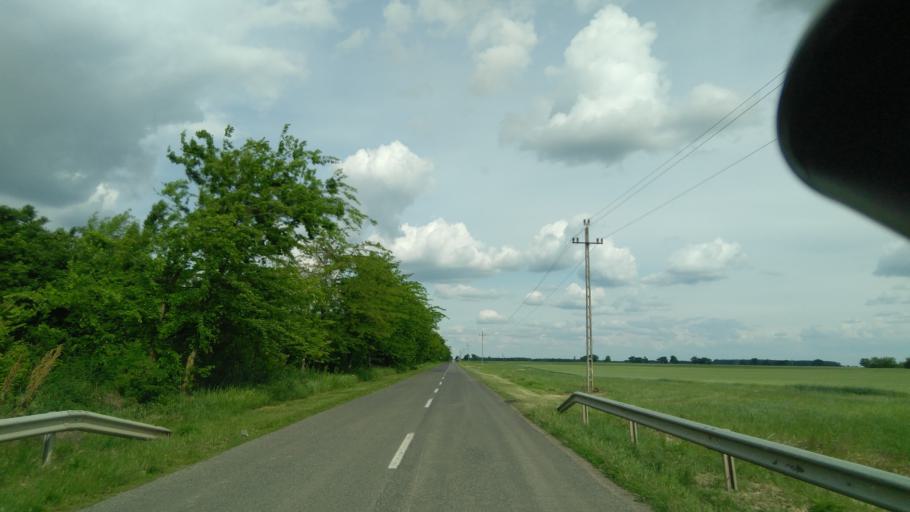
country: HU
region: Bekes
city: Mezohegyes
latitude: 46.3074
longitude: 20.8866
